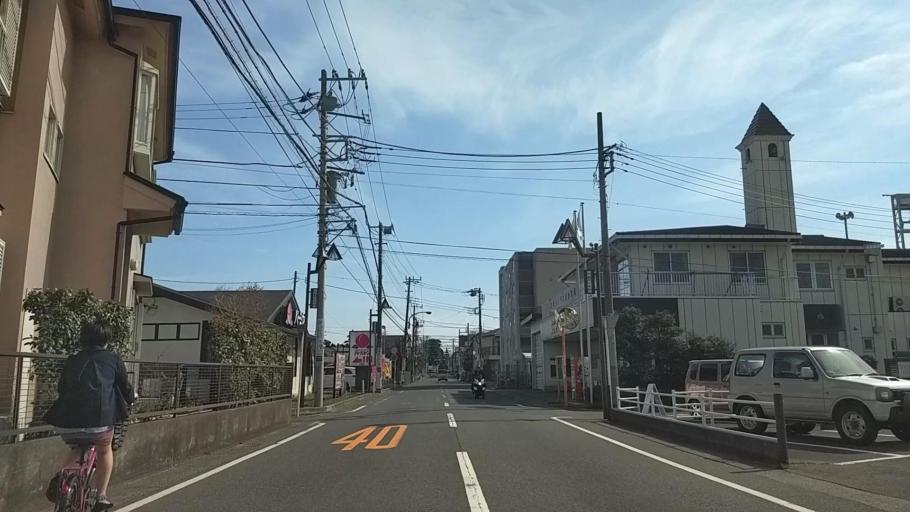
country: JP
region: Kanagawa
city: Fujisawa
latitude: 35.3297
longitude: 139.4519
